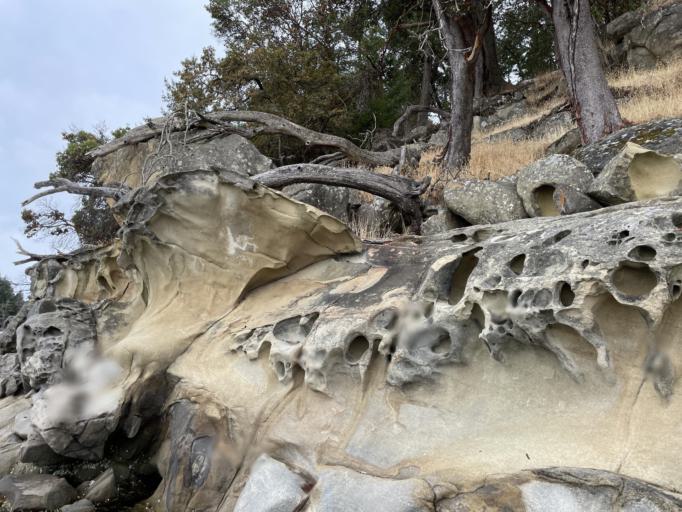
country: CA
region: British Columbia
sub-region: Cowichan Valley Regional District
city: Ladysmith
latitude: 49.0925
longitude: -123.7218
